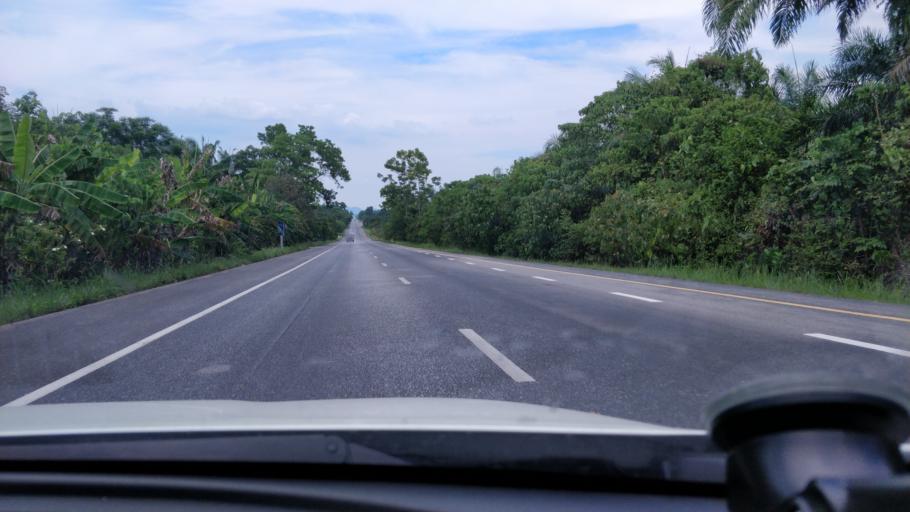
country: TH
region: Krabi
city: Plai Phraya
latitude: 8.4742
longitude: 98.8686
